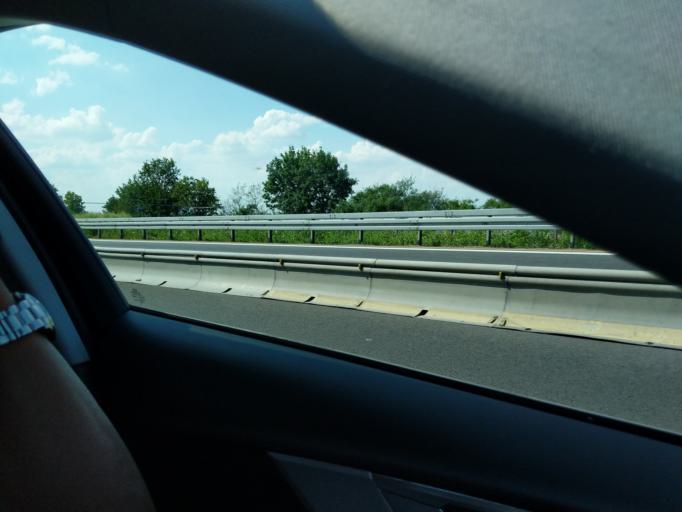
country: DE
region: Saxony
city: Rackwitz
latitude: 51.4143
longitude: 12.3319
